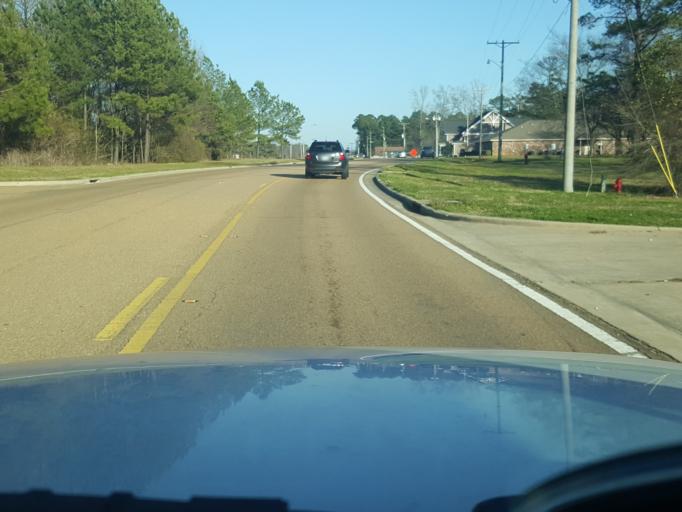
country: US
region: Mississippi
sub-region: Rankin County
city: Flowood
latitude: 32.3418
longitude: -90.0921
